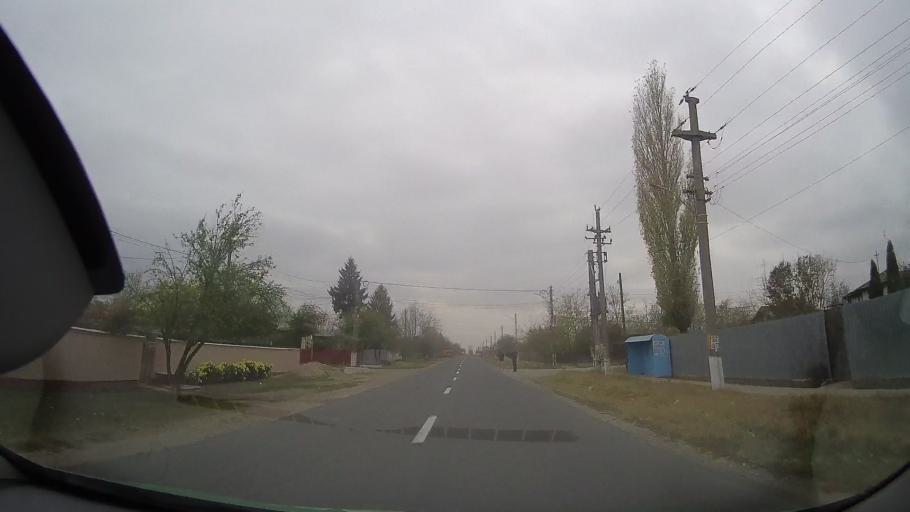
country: RO
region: Ialomita
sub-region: Comuna Garbovi
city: Garbovi
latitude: 44.7832
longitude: 26.7579
